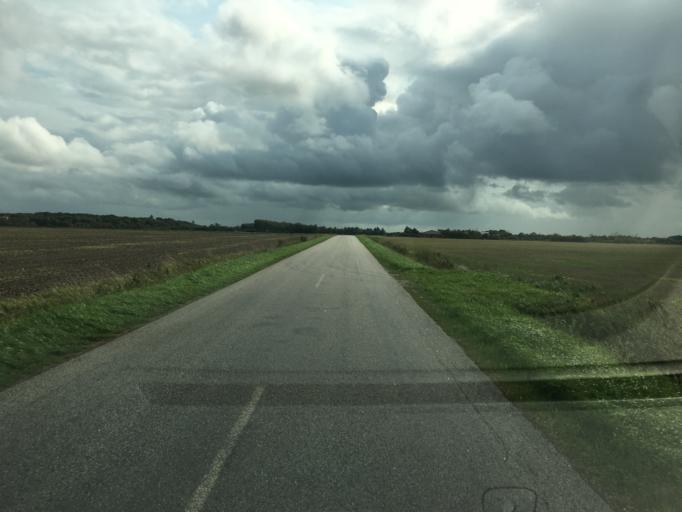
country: DK
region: South Denmark
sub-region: Tonder Kommune
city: Tonder
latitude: 54.9747
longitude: 8.8160
